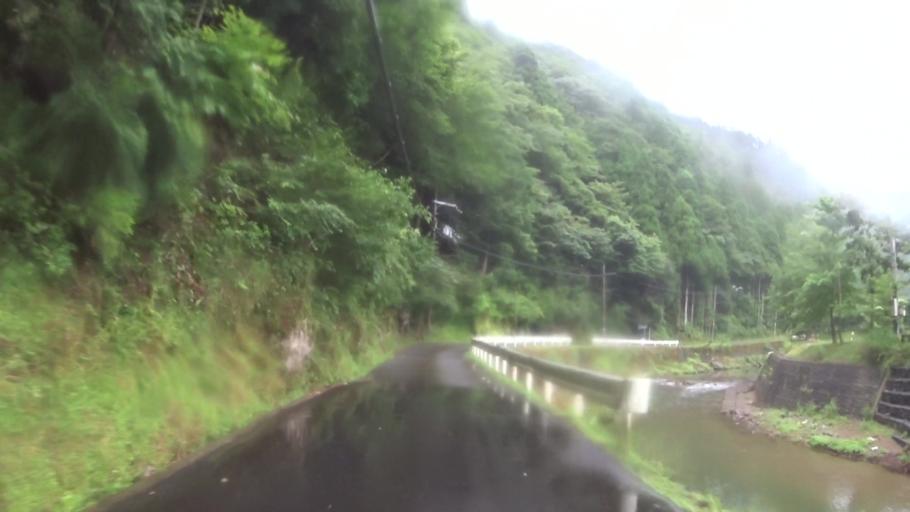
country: JP
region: Shiga Prefecture
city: Kitahama
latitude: 35.2793
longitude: 135.8465
